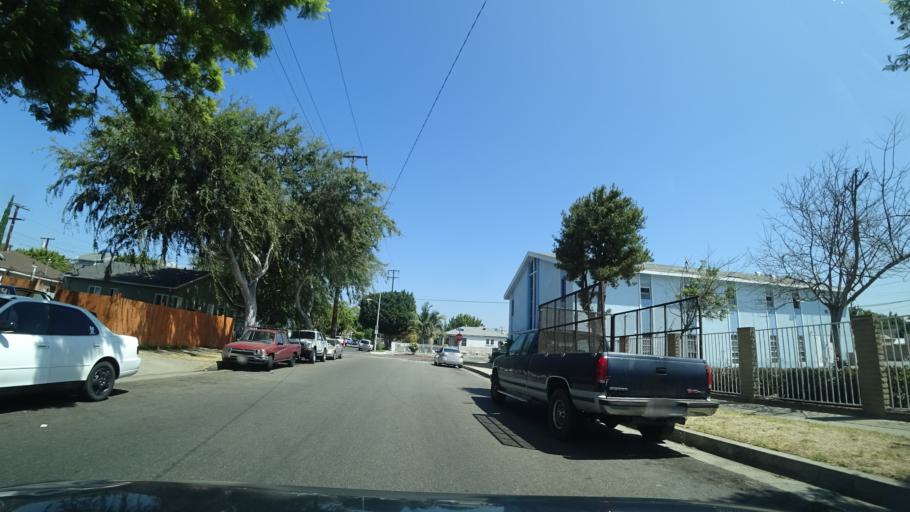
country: US
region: California
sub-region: Los Angeles County
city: Inglewood
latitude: 33.9498
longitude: -118.3667
